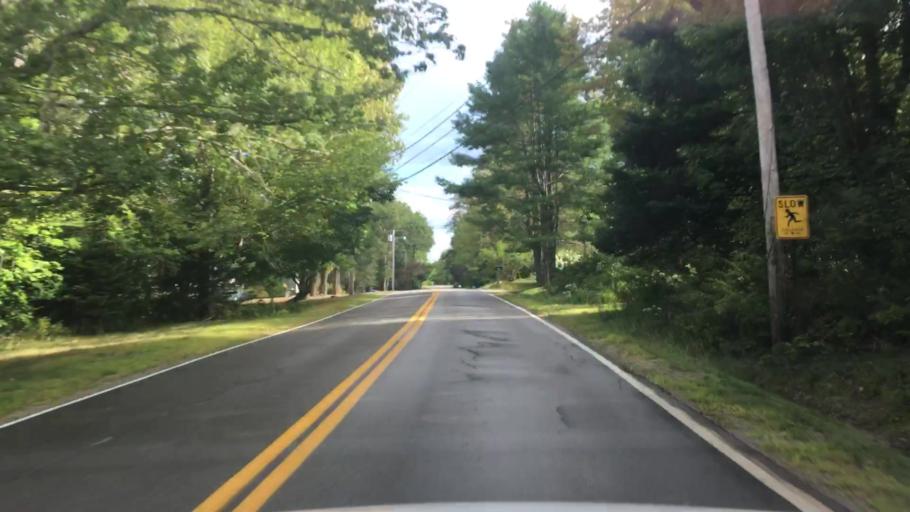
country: US
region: Maine
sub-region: Hancock County
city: Trenton
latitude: 44.4324
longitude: -68.3978
